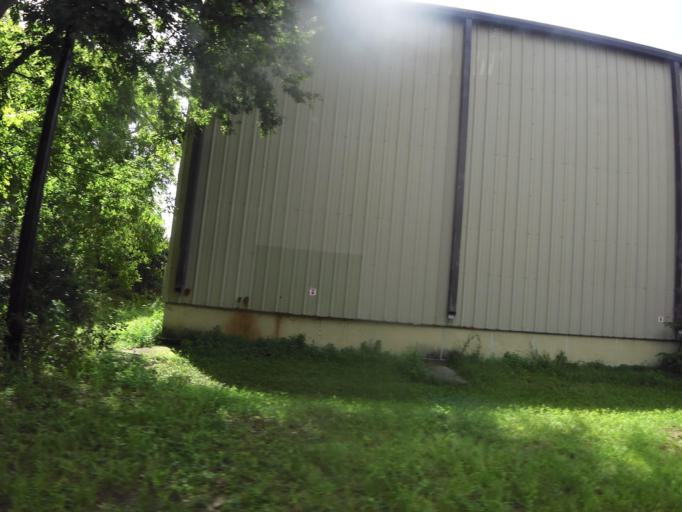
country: US
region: Florida
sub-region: Nassau County
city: Fernandina Beach
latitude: 30.6752
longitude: -81.4625
